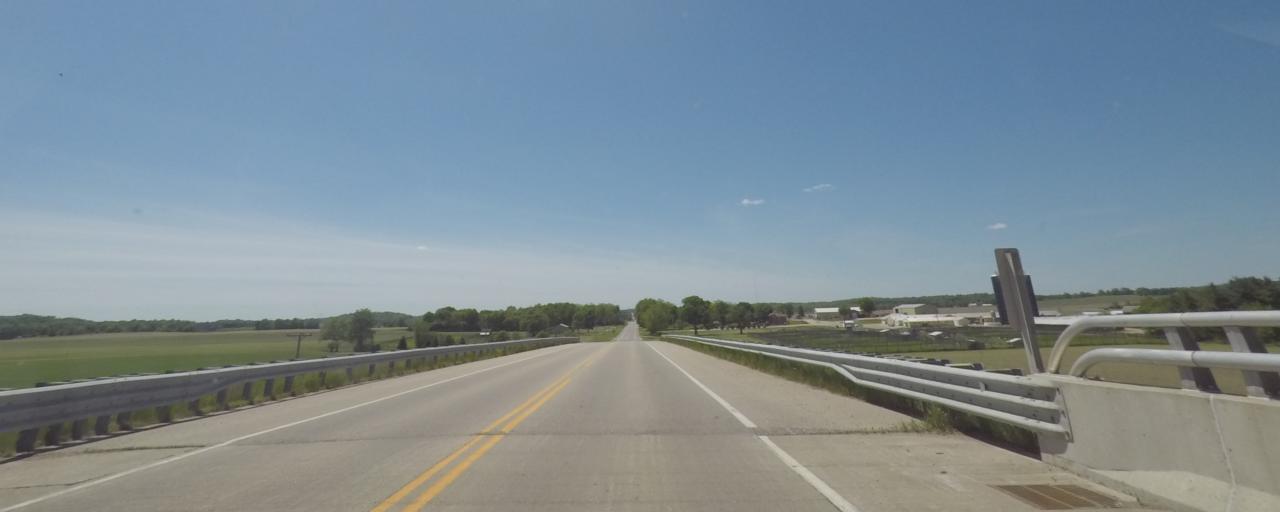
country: US
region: Wisconsin
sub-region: Dane County
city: Oregon
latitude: 42.9502
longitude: -89.3914
